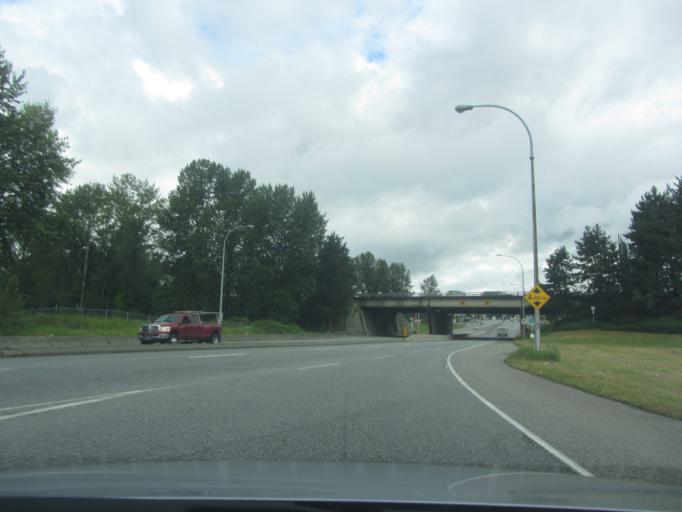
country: CA
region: British Columbia
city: Abbotsford
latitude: 49.0326
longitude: -122.2659
